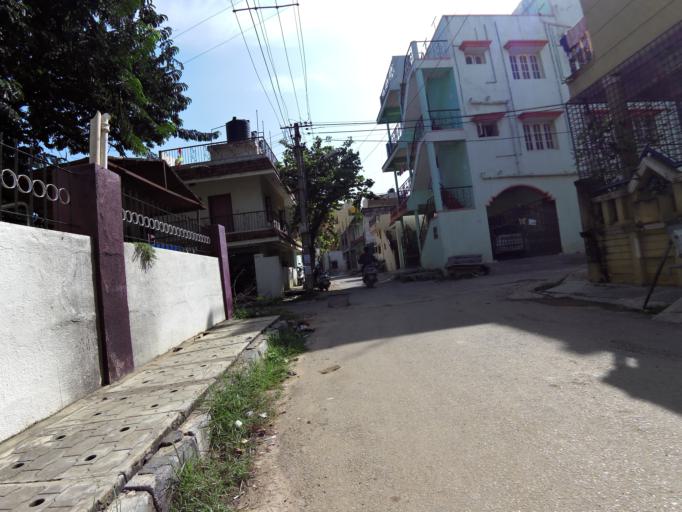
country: IN
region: Karnataka
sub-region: Bangalore Urban
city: Bangalore
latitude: 13.0036
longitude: 77.6335
